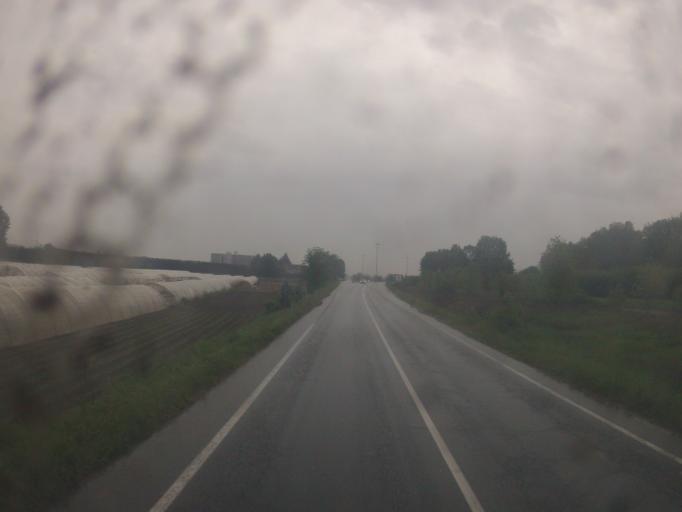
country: IT
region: Piedmont
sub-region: Provincia di Torino
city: La Loggia
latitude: 44.9371
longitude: 7.6711
